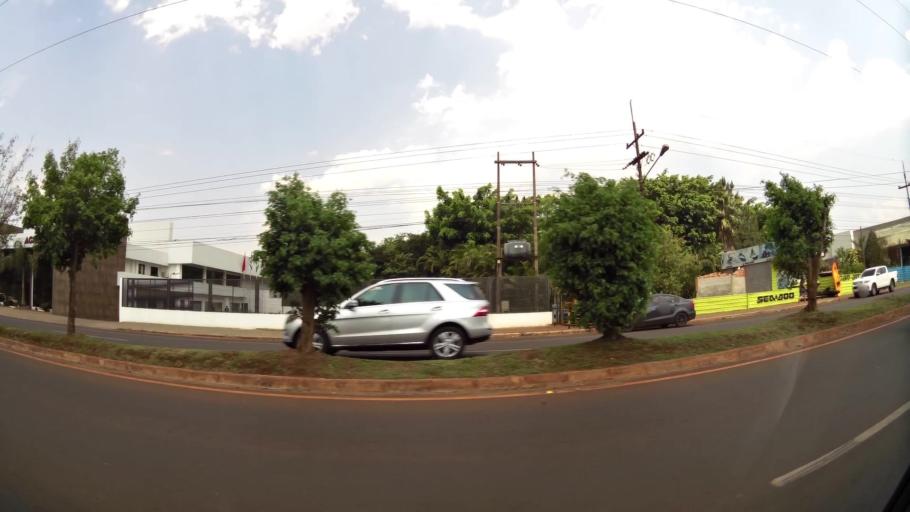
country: PY
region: Alto Parana
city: Ciudad del Este
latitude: -25.4964
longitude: -54.6343
